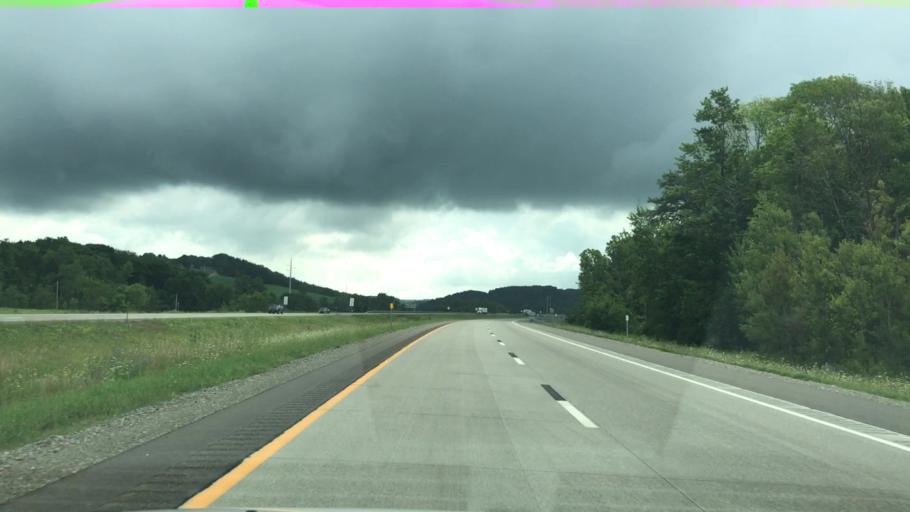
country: US
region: New York
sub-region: Steuben County
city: Wayland
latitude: 42.5410
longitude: -77.5766
